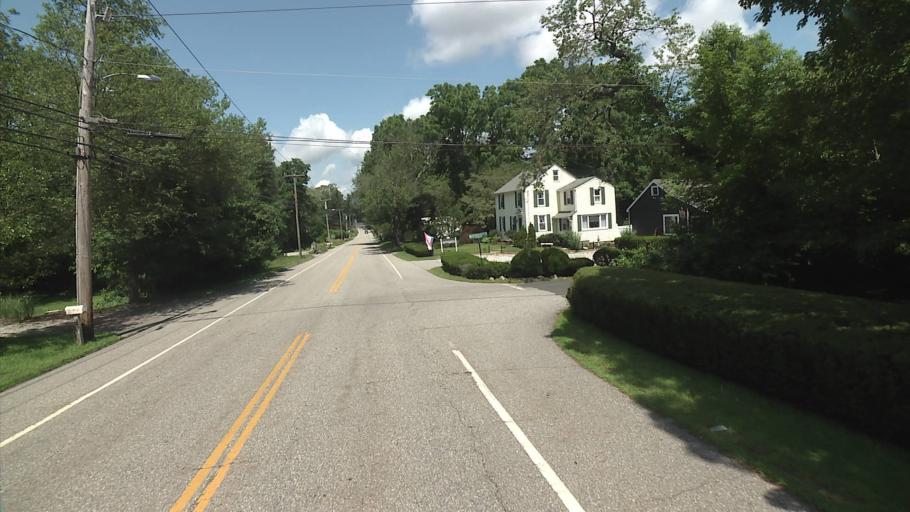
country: US
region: Connecticut
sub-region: Middlesex County
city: Essex Village
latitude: 41.3329
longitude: -72.3806
